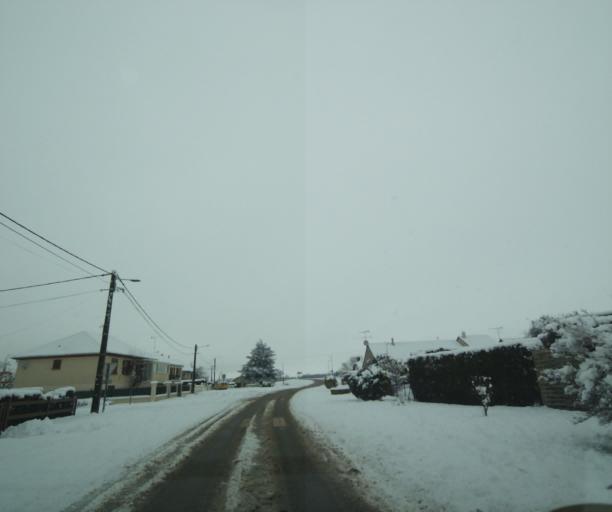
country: FR
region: Champagne-Ardenne
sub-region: Departement de la Haute-Marne
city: Wassy
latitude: 48.5626
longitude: 4.8959
